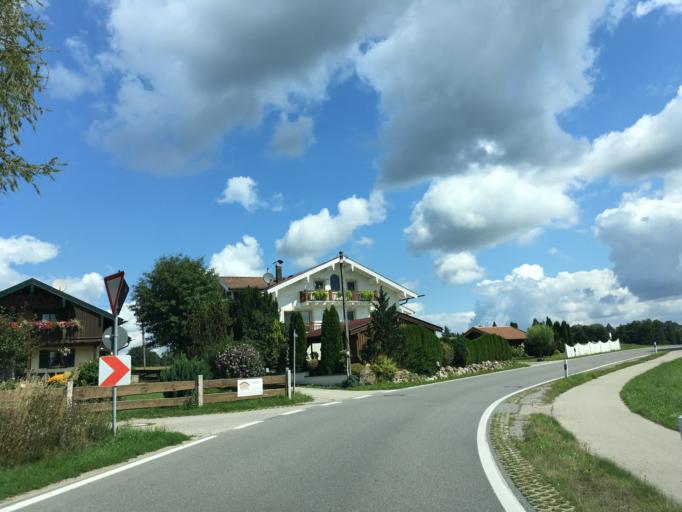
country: DE
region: Bavaria
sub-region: Upper Bavaria
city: Eggstatt
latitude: 47.9379
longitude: 12.3707
